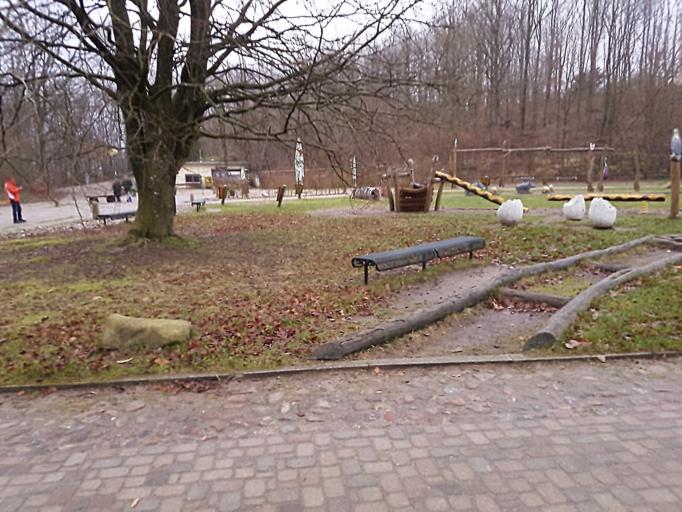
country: DE
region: Mecklenburg-Vorpommern
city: Ostseebad Binz
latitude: 54.3821
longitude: 13.6282
